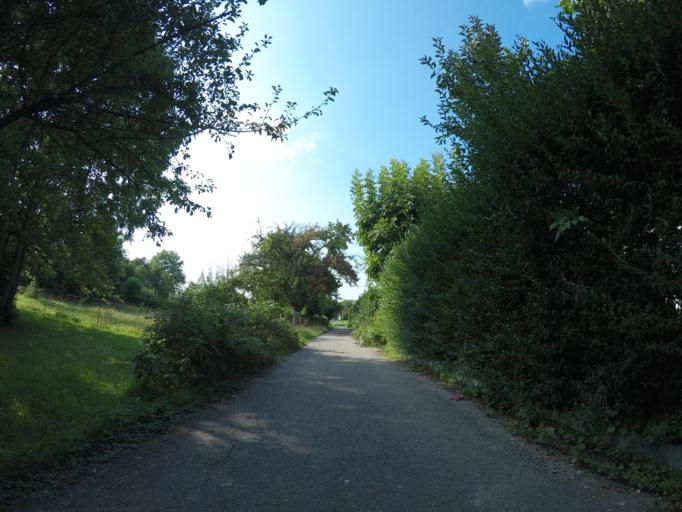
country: DE
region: Baden-Wuerttemberg
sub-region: Tuebingen Region
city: Reutlingen
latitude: 48.4848
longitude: 9.1805
